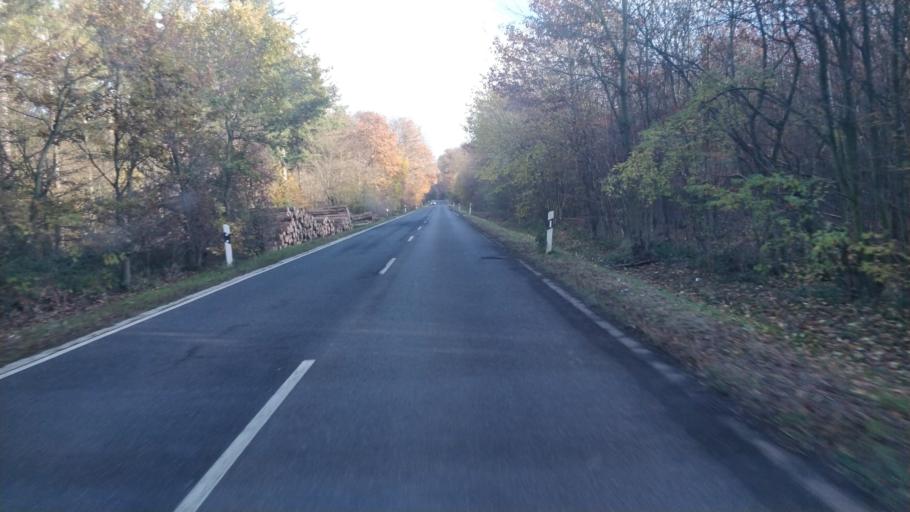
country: DE
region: North Rhine-Westphalia
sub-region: Regierungsbezirk Koln
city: Rheinbach
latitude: 50.6194
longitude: 6.8807
